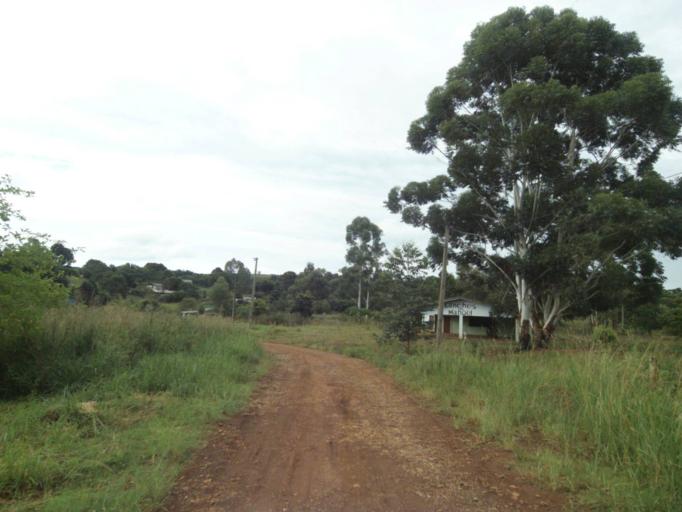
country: BR
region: Parana
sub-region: Pitanga
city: Pitanga
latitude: -24.8985
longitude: -51.9639
